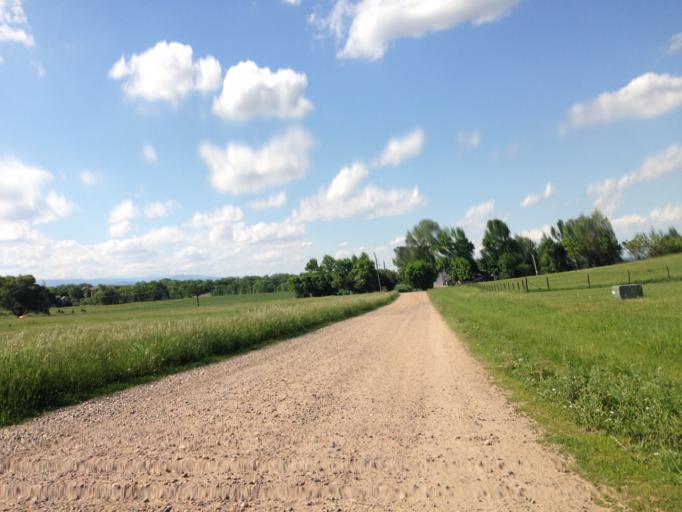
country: US
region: Colorado
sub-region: Boulder County
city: Lafayette
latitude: 40.0131
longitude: -105.1157
